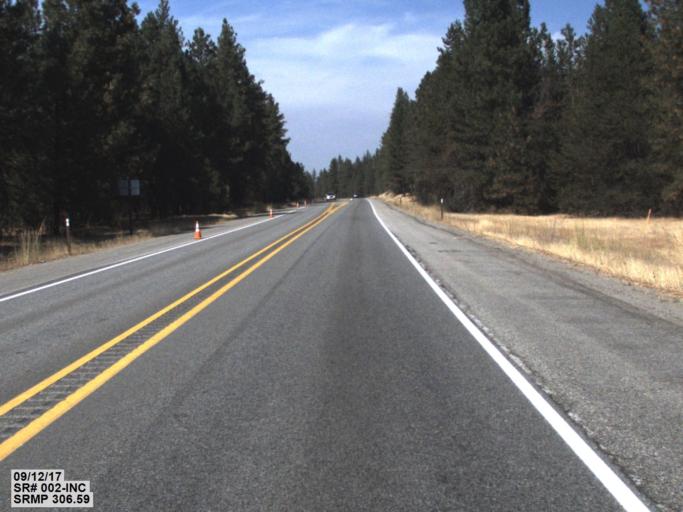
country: US
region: Washington
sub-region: Spokane County
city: Deer Park
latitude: 47.9198
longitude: -117.3501
